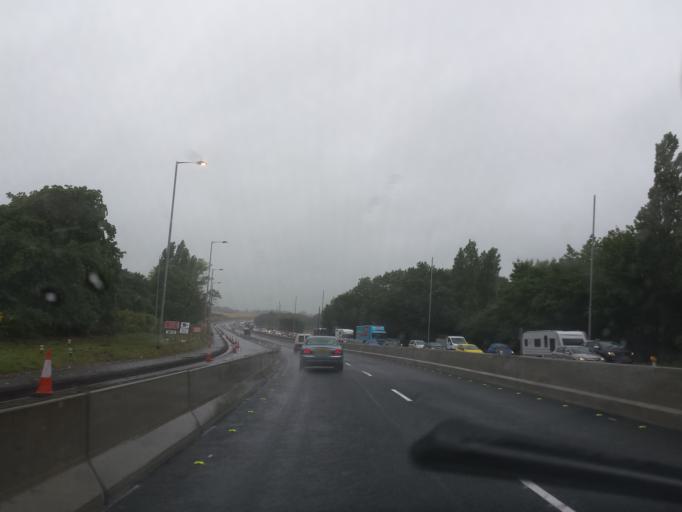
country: GB
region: England
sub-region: Warwickshire
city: Ryton on Dunsmore
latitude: 52.3791
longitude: -1.4740
